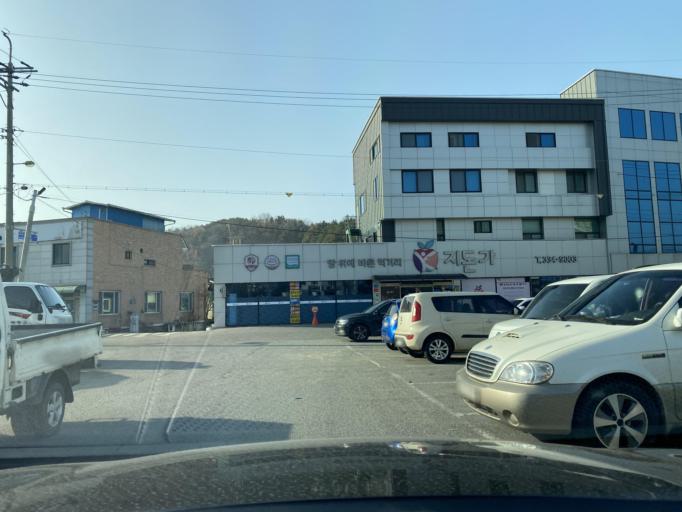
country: KR
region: Chungcheongnam-do
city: Yesan
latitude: 36.6810
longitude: 126.8328
